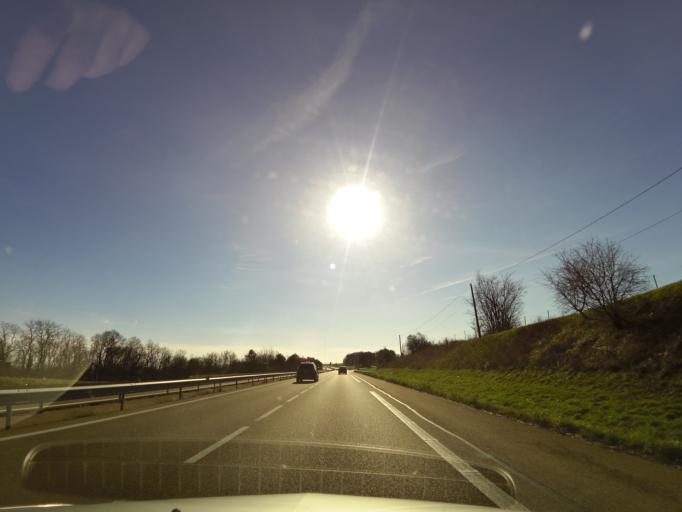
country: FR
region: Bourgogne
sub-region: Departement de l'Yonne
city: Saint-Bris-le-Vineux
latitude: 47.7562
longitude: 3.7289
